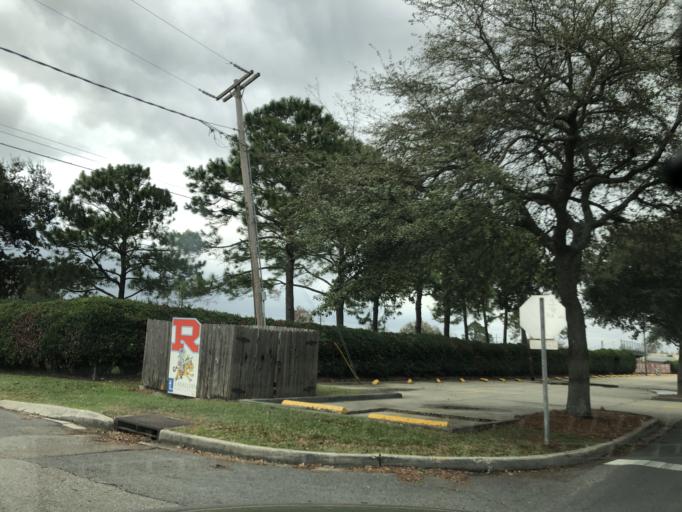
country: US
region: Louisiana
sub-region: Jefferson Parish
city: Metairie
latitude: 29.9893
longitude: -90.1600
